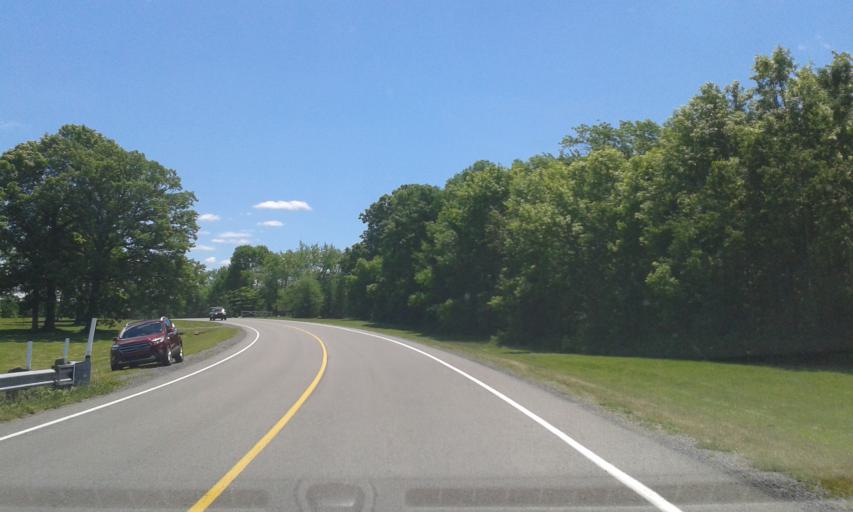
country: US
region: New York
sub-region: St. Lawrence County
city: Massena
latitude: 44.9925
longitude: -74.9704
